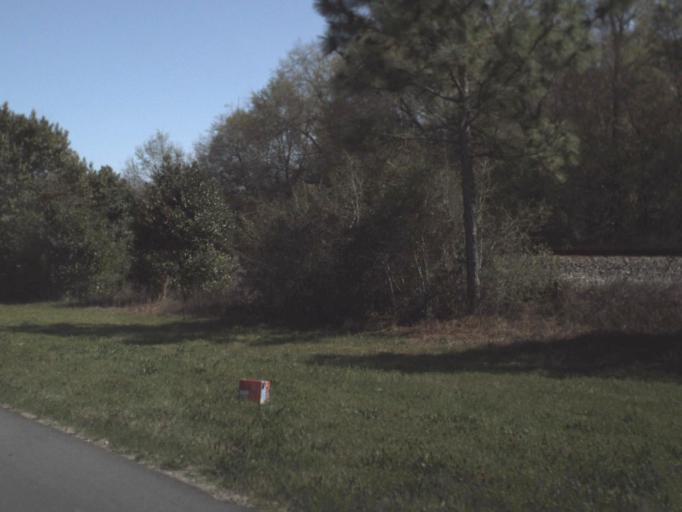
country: US
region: Florida
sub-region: Walton County
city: DeFuniak Springs
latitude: 30.7386
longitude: -86.1741
